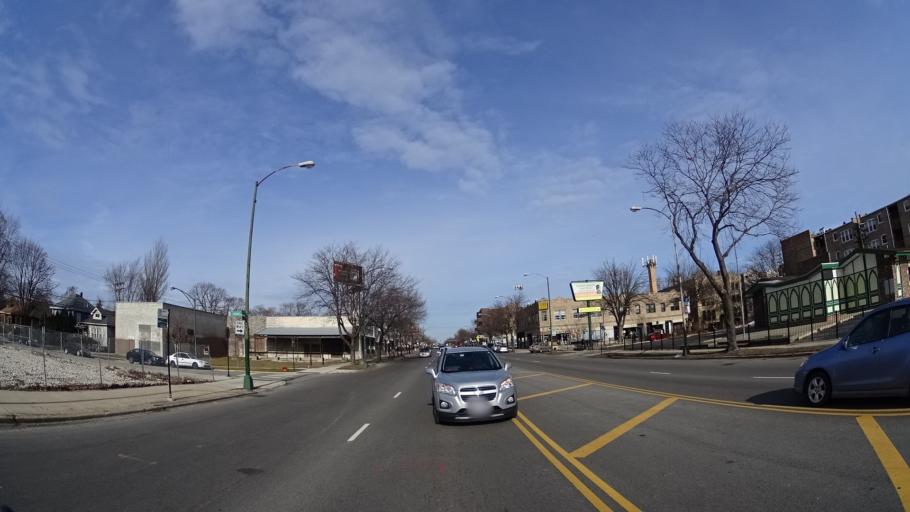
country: US
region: Illinois
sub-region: Cook County
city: Evanston
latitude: 42.0057
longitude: -87.6901
